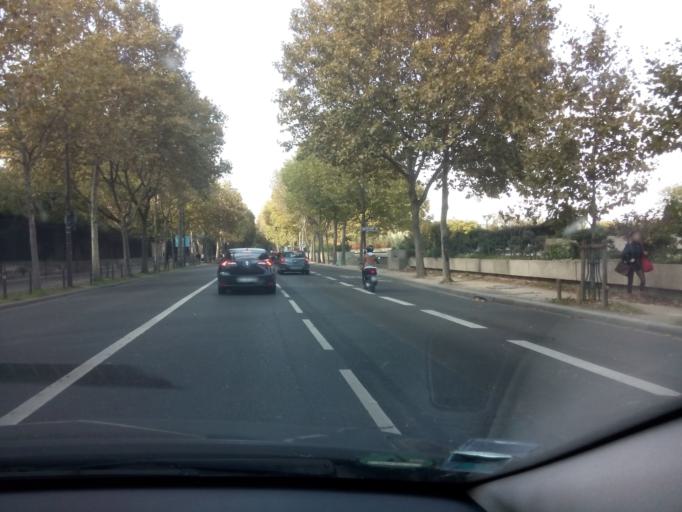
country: FR
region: Ile-de-France
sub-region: Paris
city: Paris
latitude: 48.8460
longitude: 2.3622
